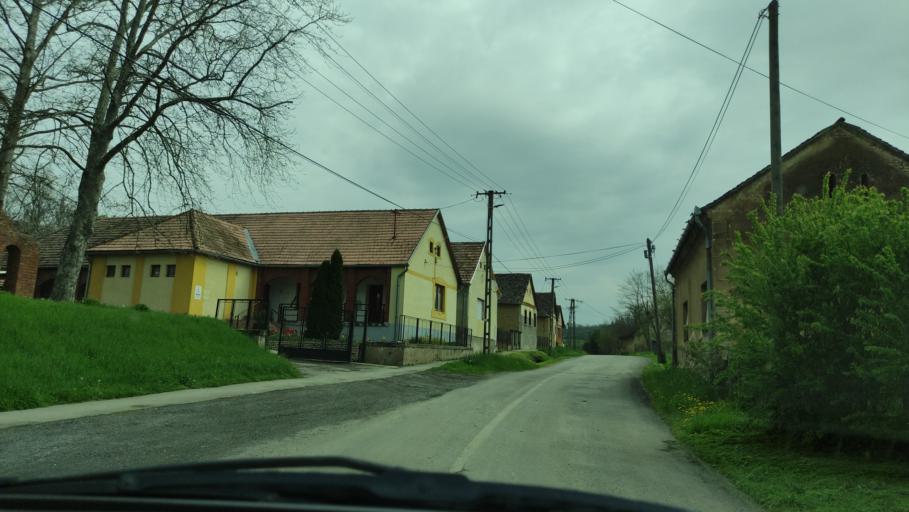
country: HU
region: Baranya
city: Magocs
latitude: 46.3058
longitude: 18.1849
